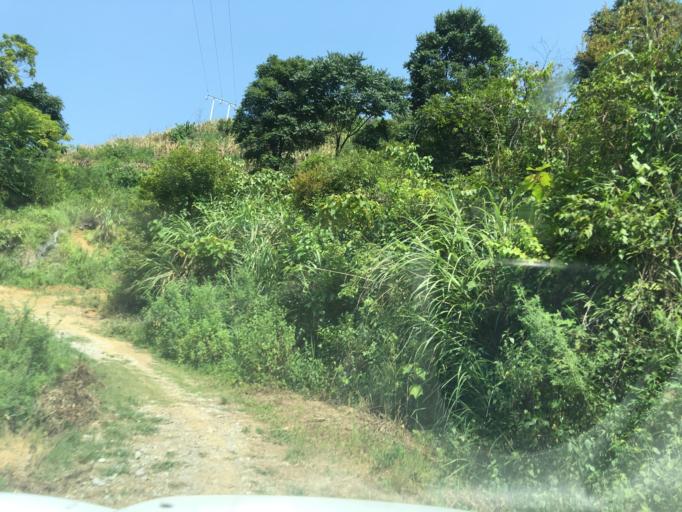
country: CN
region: Guangxi Zhuangzu Zizhiqu
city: Xinzhou
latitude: 24.9916
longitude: 105.7437
